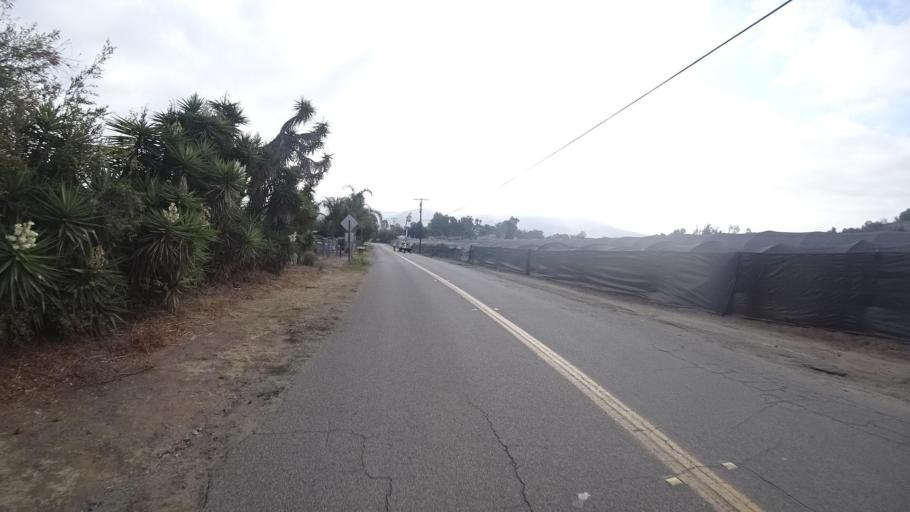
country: US
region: California
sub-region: San Diego County
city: San Marcos
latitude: 33.1794
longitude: -117.1658
